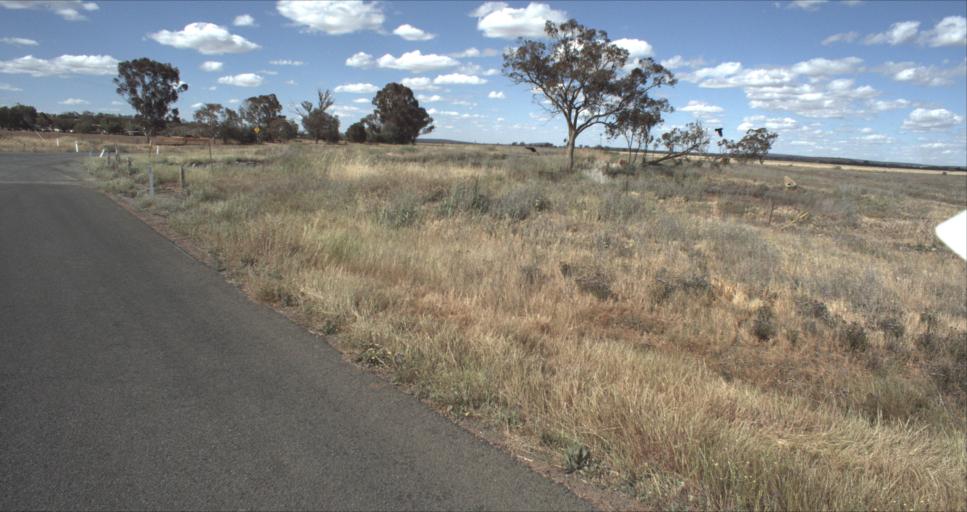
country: AU
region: New South Wales
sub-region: Leeton
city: Leeton
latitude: -34.4285
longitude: 146.2587
